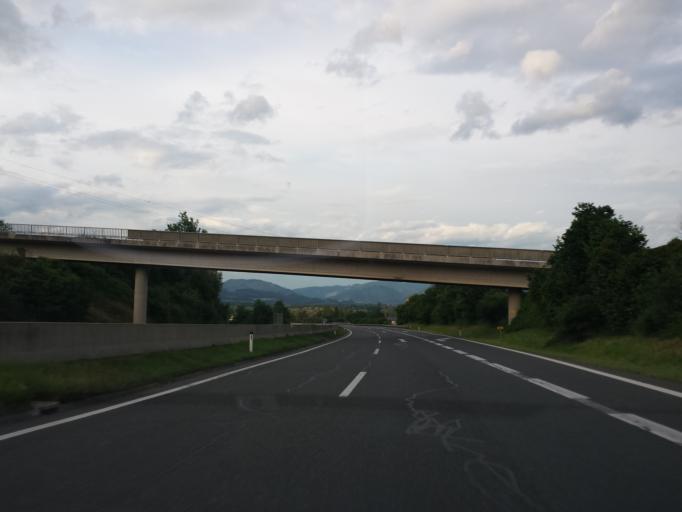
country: AT
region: Styria
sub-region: Politischer Bezirk Murtal
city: Knittelfeld
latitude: 47.2267
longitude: 14.8258
